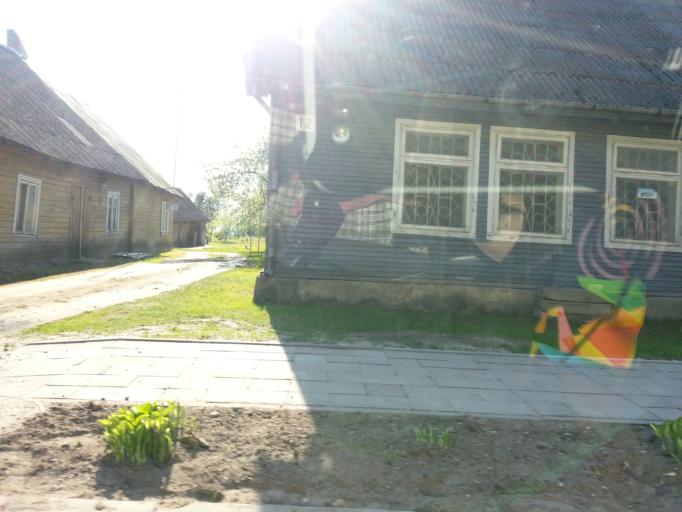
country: LT
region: Panevezys
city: Pasvalys
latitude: 55.9356
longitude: 24.3401
